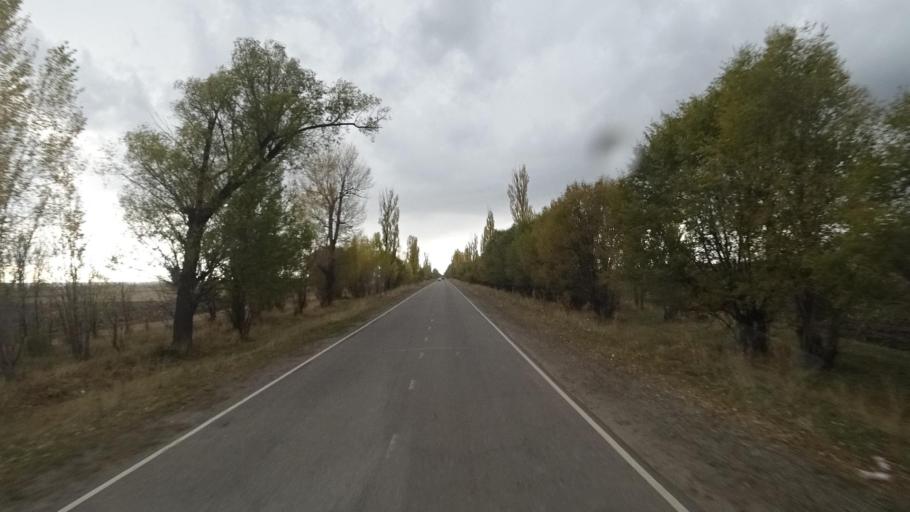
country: KG
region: Ysyk-Koel
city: Tyup
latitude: 42.7457
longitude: 78.4236
